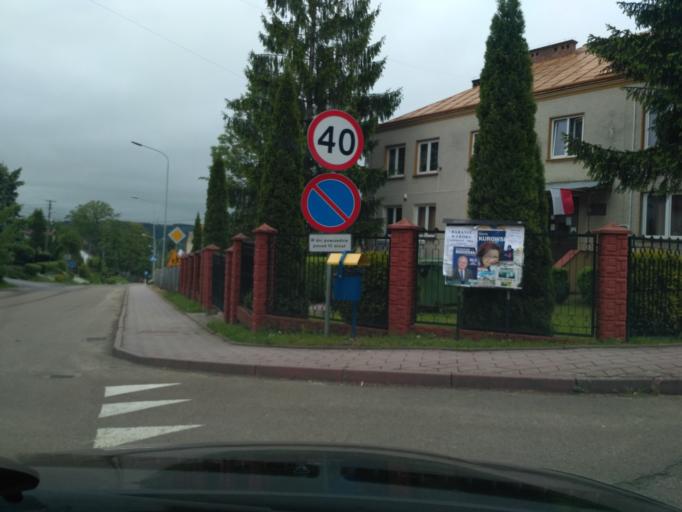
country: PL
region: Subcarpathian Voivodeship
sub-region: Powiat jasielski
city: Brzyska
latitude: 49.8185
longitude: 21.3876
